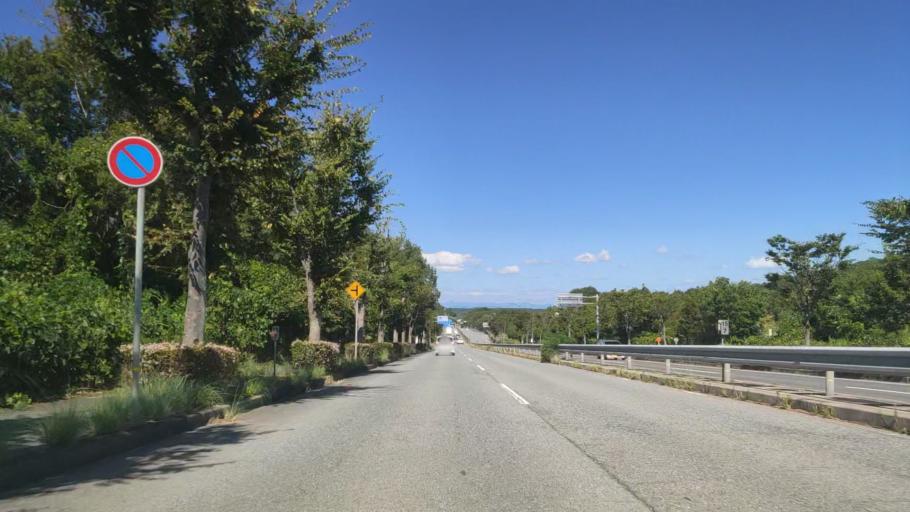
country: JP
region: Hyogo
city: Miki
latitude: 34.7858
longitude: 134.9769
